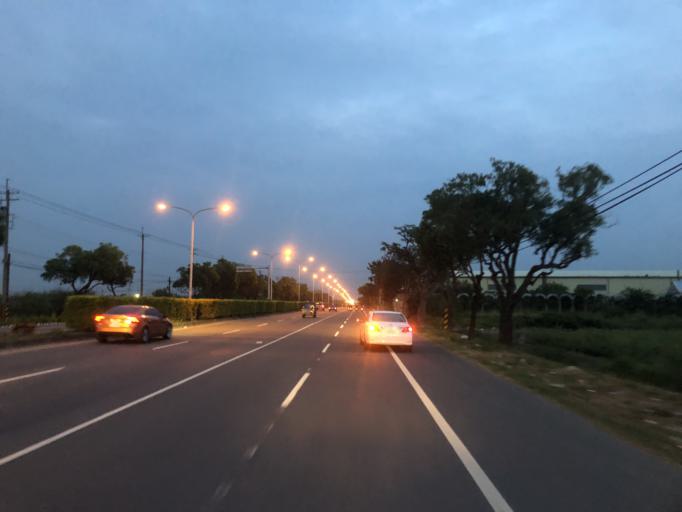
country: TW
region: Taiwan
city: Yujing
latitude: 23.1447
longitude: 120.3279
